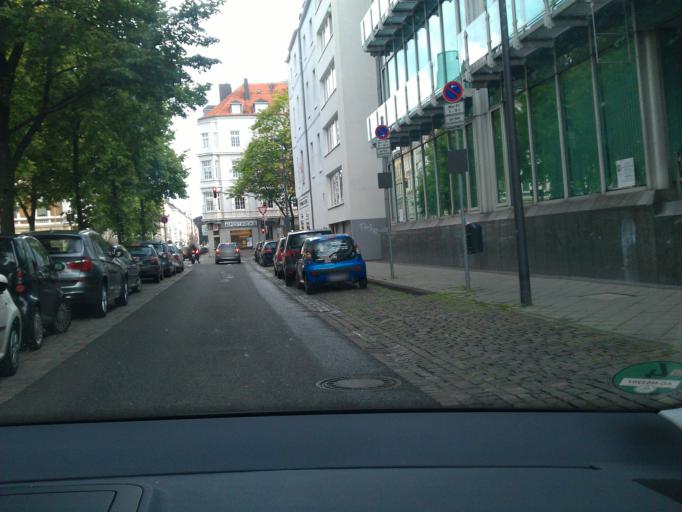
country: DE
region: North Rhine-Westphalia
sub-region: Regierungsbezirk Koln
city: Aachen
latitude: 50.7696
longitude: 6.1082
